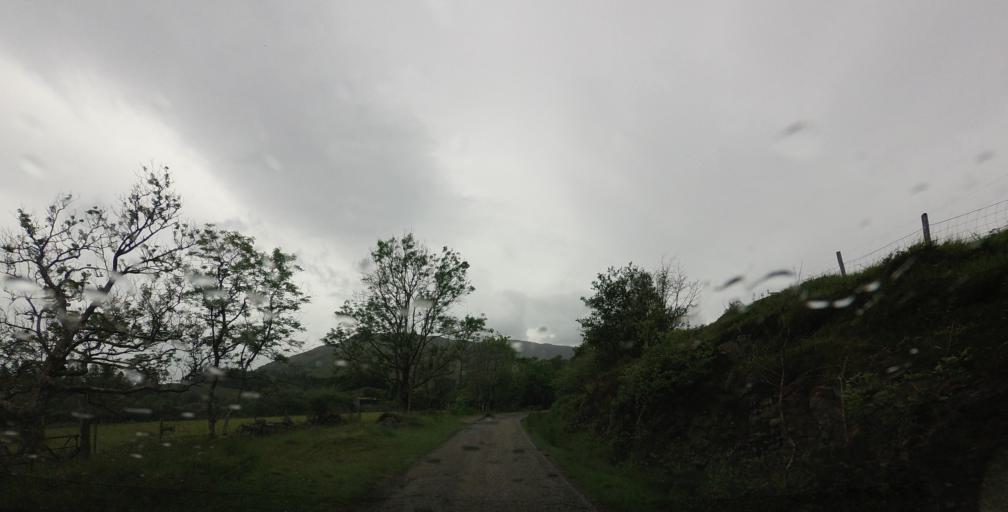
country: GB
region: Scotland
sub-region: Highland
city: Fort William
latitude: 56.8043
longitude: -5.1580
